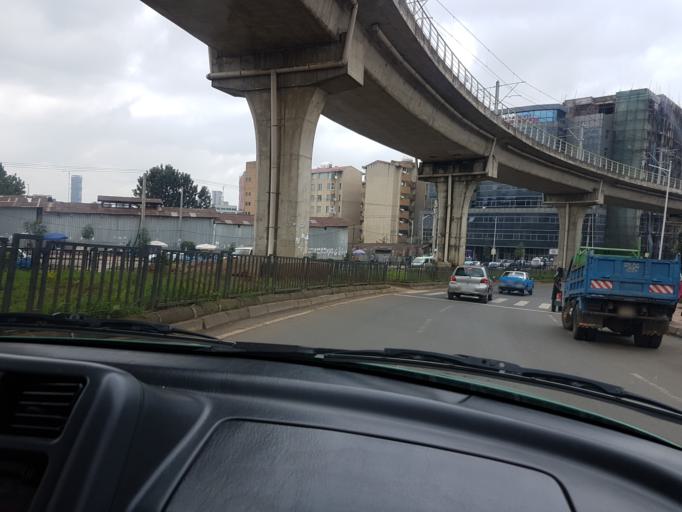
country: ET
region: Adis Abeba
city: Addis Ababa
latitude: 9.0187
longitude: 38.7346
